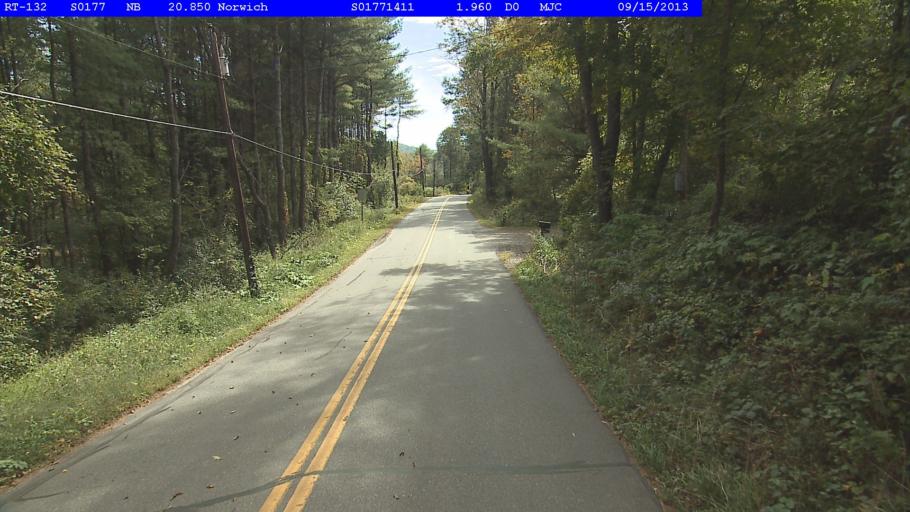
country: US
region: New Hampshire
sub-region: Grafton County
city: Hanover
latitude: 43.7643
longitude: -72.2418
